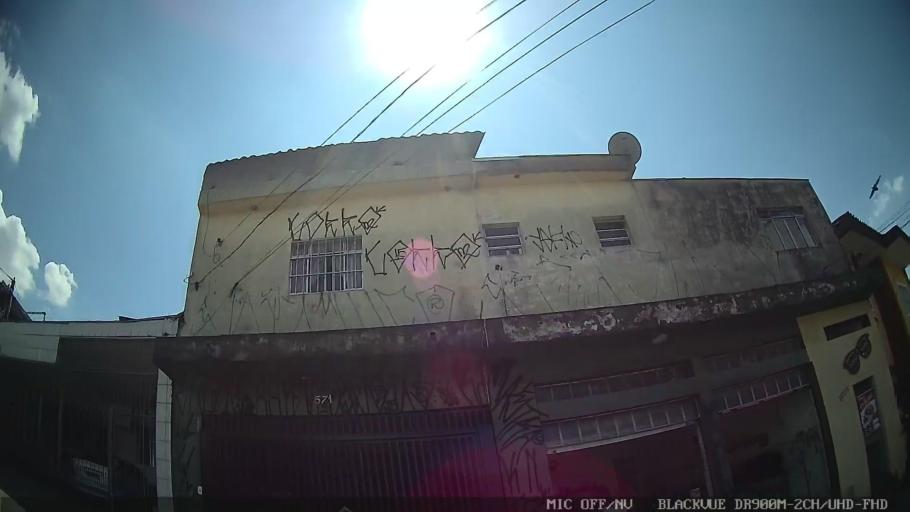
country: BR
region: Sao Paulo
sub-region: Guarulhos
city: Guarulhos
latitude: -23.5000
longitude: -46.5132
